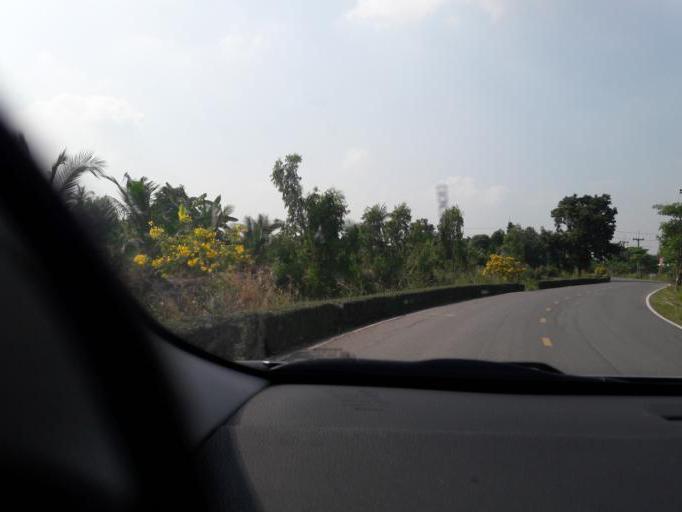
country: TH
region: Ang Thong
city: Wiset Chaichan
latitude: 14.5341
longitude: 100.3733
